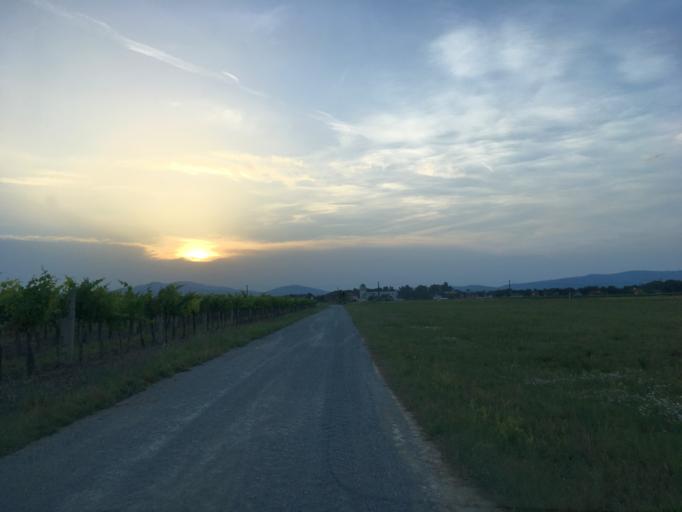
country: AT
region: Lower Austria
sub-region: Politischer Bezirk Baden
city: Tattendorf
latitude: 47.9444
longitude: 16.2954
